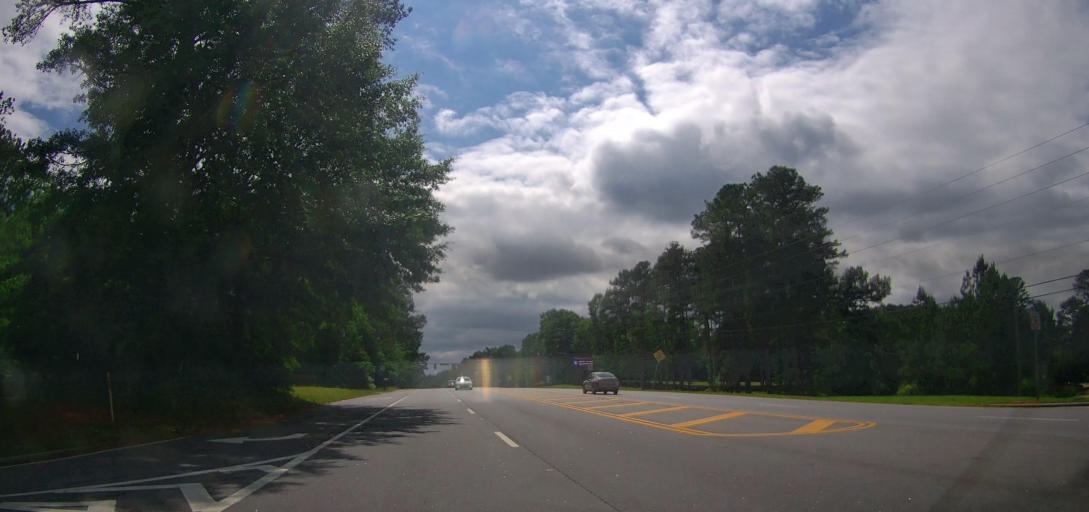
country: US
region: Georgia
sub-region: Rockdale County
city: Conyers
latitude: 33.6247
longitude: -84.0476
